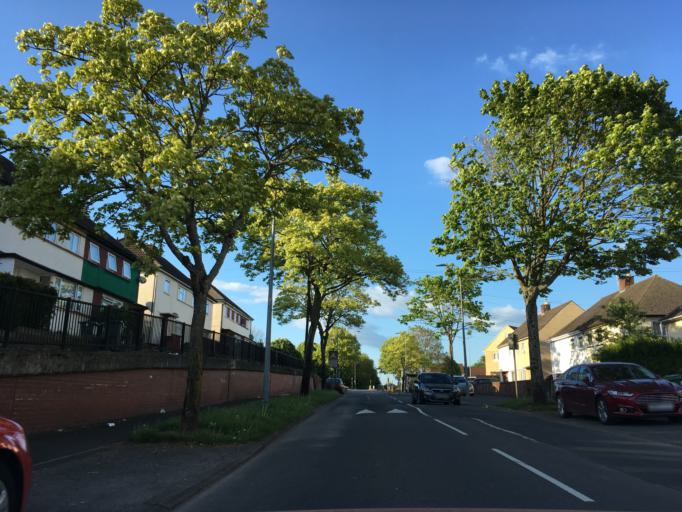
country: GB
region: Wales
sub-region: Newport
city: Marshfield
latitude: 51.5138
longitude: -3.1156
